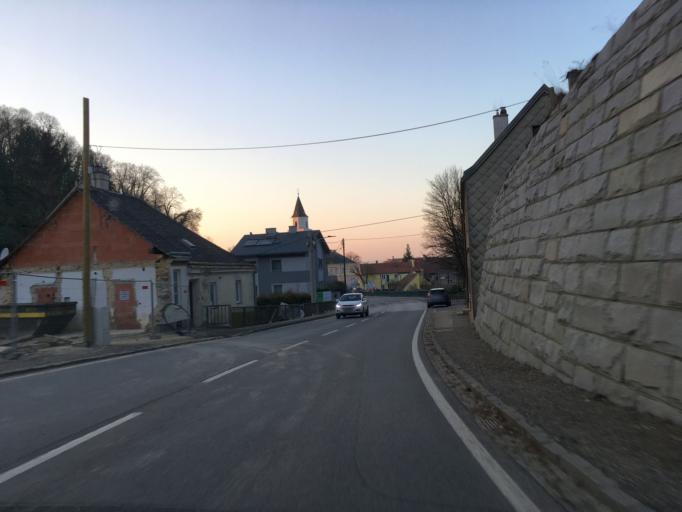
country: AT
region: Lower Austria
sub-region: Politischer Bezirk Tulln
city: Wordern
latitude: 48.3195
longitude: 16.2094
